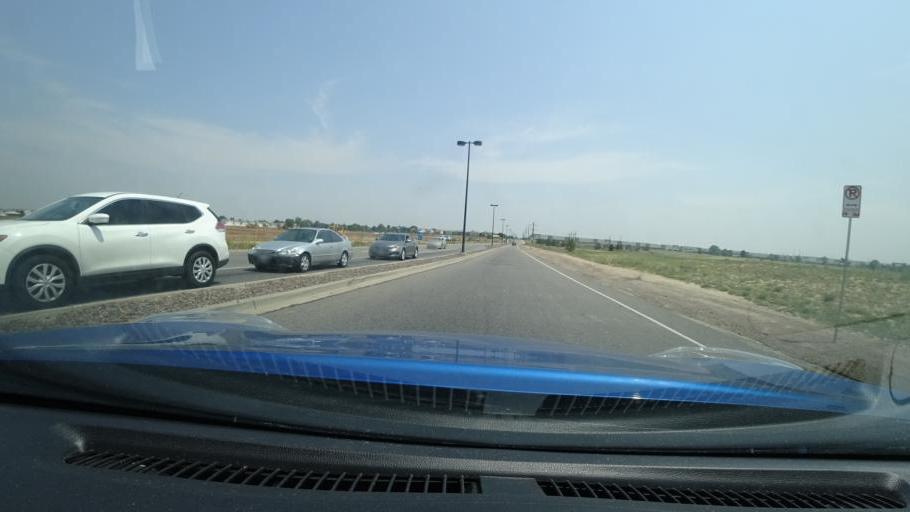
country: US
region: Colorado
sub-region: Adams County
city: Aurora
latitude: 39.7693
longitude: -104.7715
